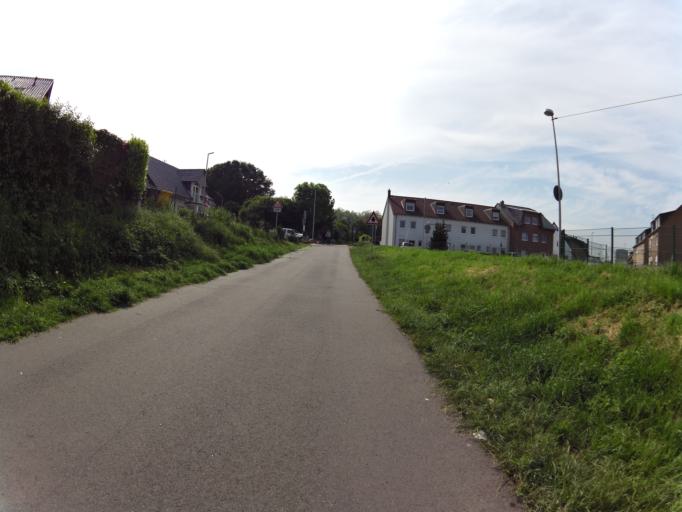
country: DE
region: North Rhine-Westphalia
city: Siersdorf
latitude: 50.8654
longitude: 6.2066
